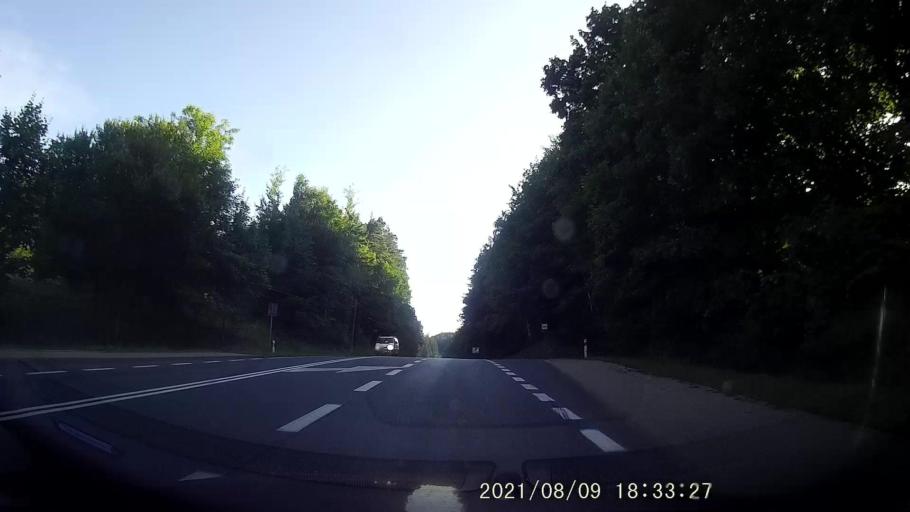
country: PL
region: Lower Silesian Voivodeship
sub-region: Powiat zabkowicki
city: Bardo
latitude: 50.4902
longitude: 16.7209
